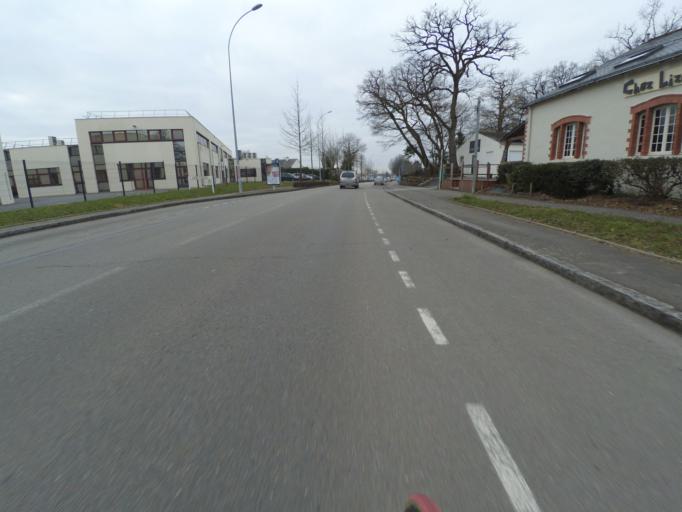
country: FR
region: Pays de la Loire
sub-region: Departement de la Loire-Atlantique
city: Sainte-Luce-sur-Loire
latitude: 47.2690
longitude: -1.4868
